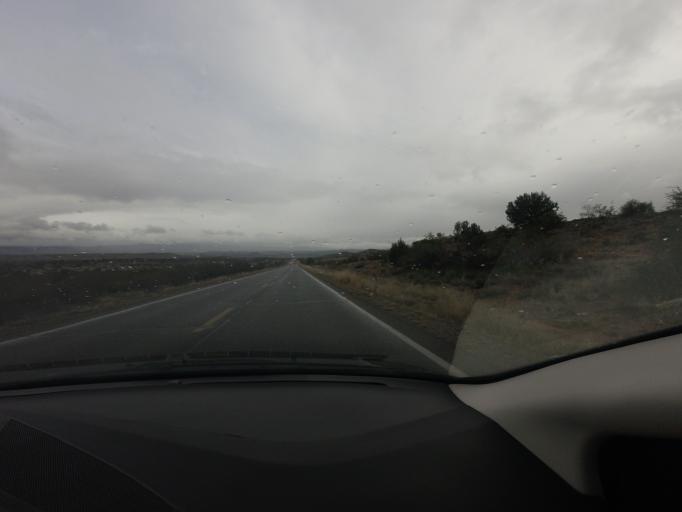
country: US
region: Arizona
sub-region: Yavapai County
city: Cornville
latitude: 34.6828
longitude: -111.8454
